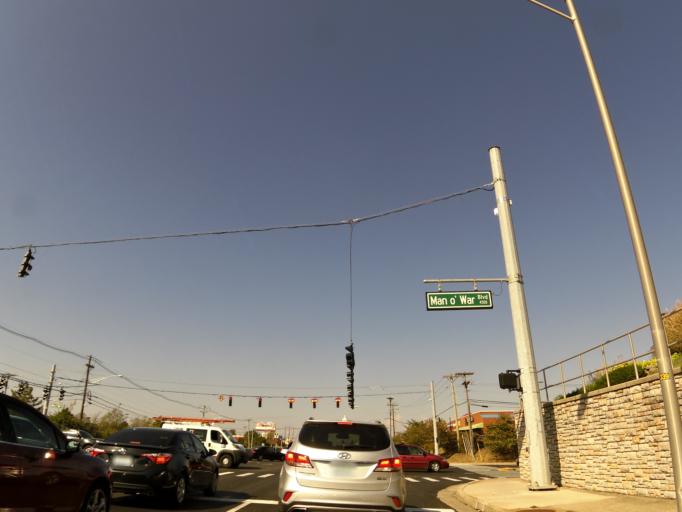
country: US
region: Kentucky
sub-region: Fayette County
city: Lexington
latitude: 38.0010
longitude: -84.4454
